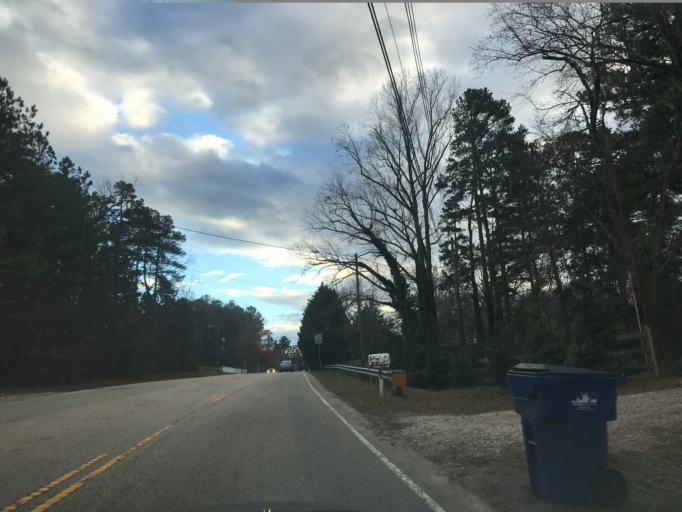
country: US
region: North Carolina
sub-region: Wake County
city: West Raleigh
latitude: 35.8506
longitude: -78.6728
